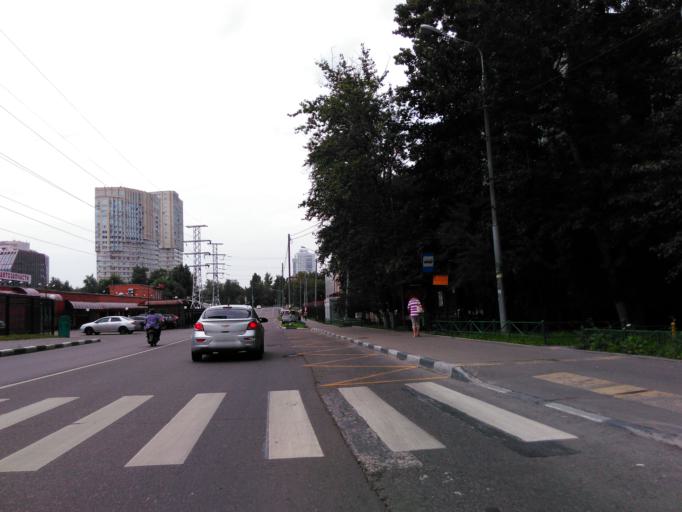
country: RU
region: Moskovskaya
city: Semenovskoye
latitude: 55.6798
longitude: 37.5532
